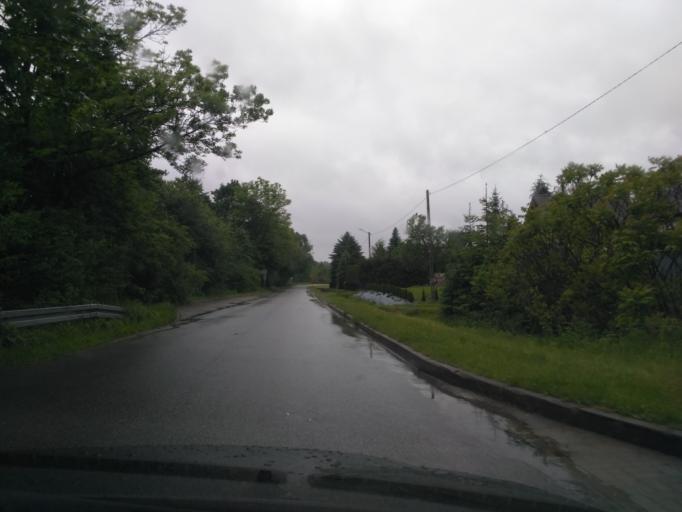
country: PL
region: Lesser Poland Voivodeship
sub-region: Powiat gorlicki
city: Sekowa
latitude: 49.6165
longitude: 21.2076
